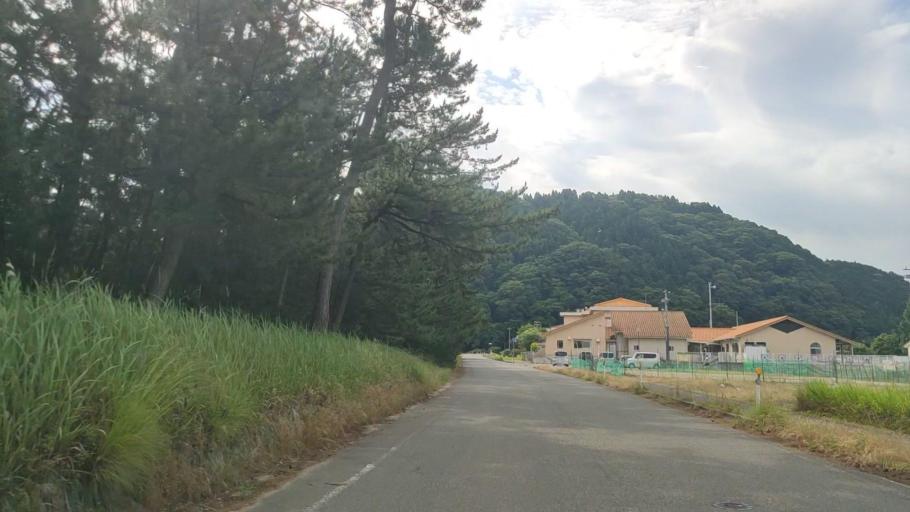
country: JP
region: Hyogo
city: Toyooka
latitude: 35.6422
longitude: 134.8377
